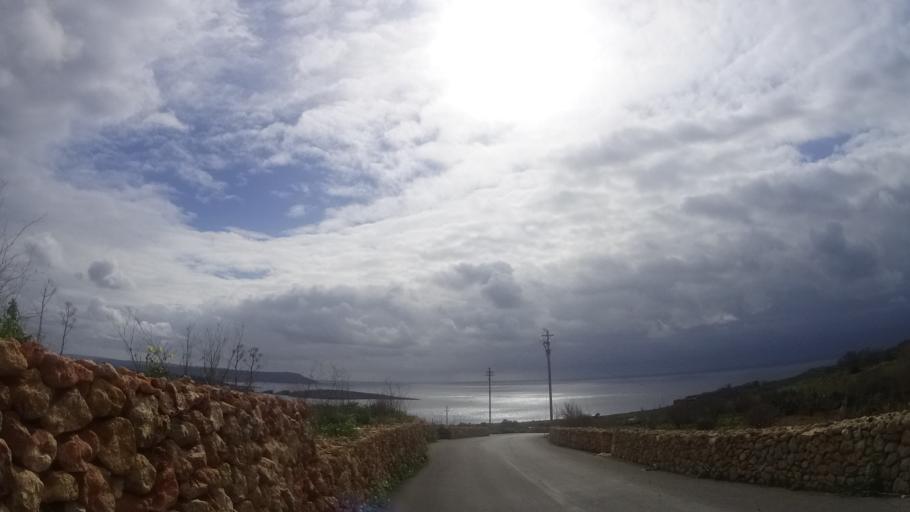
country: MT
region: Il-Qala
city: Qala
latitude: 36.0316
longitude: 14.3216
